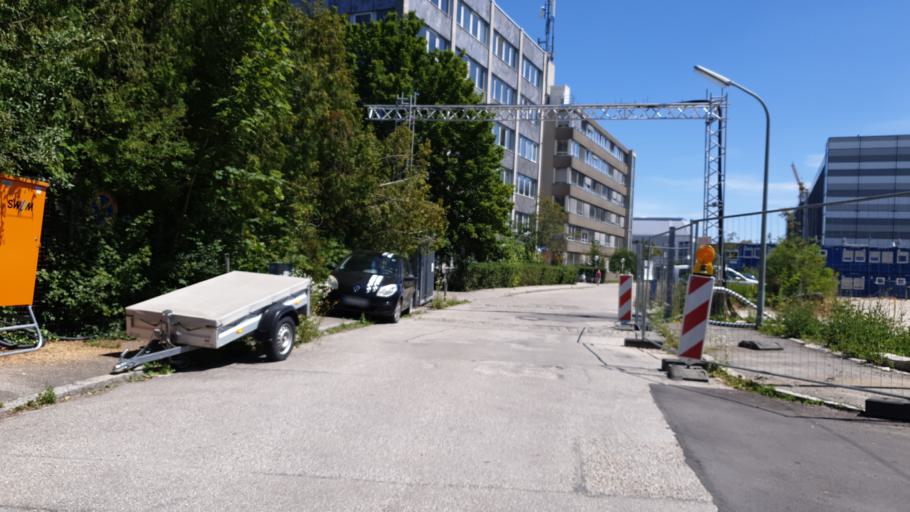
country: DE
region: Bavaria
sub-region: Upper Bavaria
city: Grafelfing
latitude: 48.1393
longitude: 11.4279
